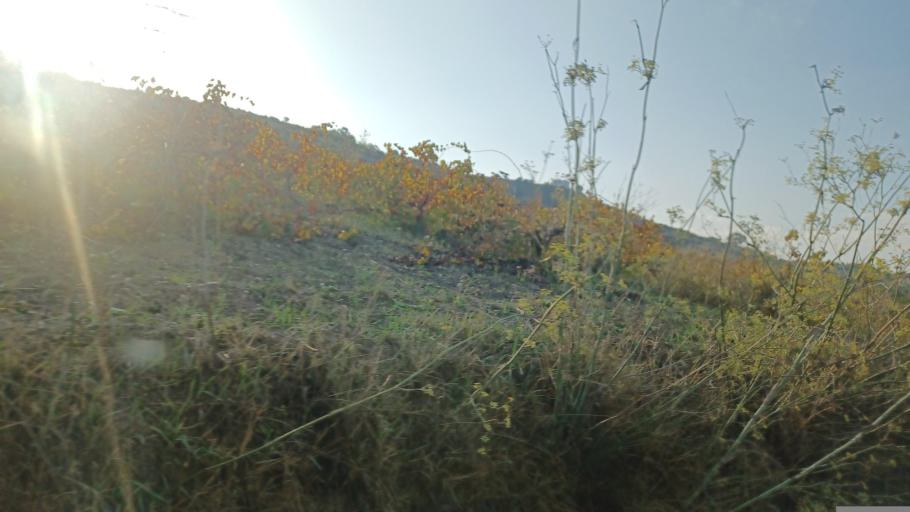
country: CY
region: Pafos
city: Tala
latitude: 34.9009
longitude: 32.4872
